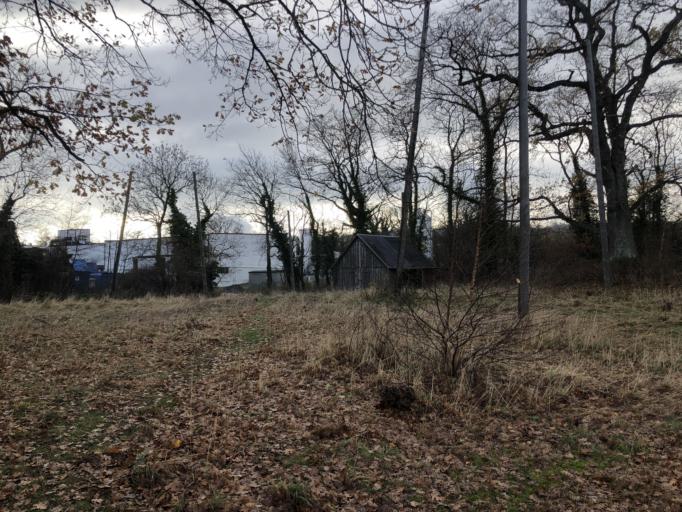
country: SE
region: Skane
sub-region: Simrishamns Kommun
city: Kivik
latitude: 55.6750
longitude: 14.2689
